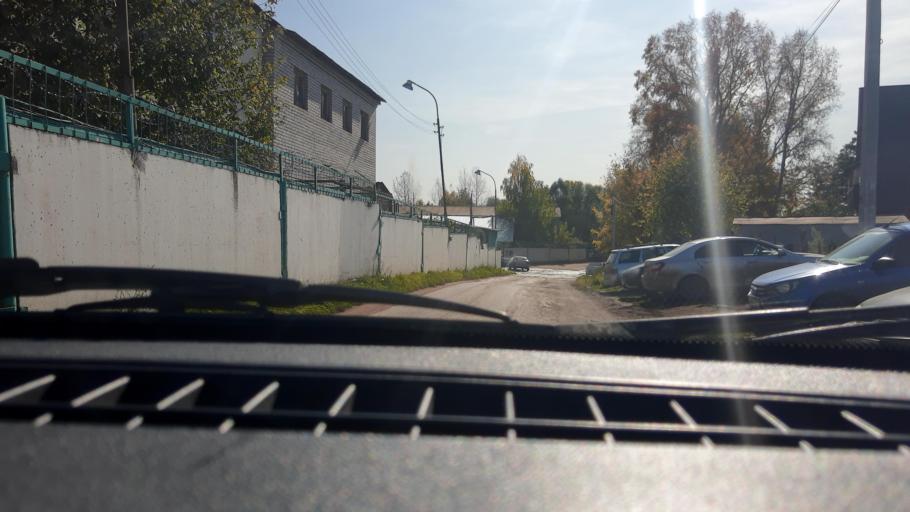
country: RU
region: Bashkortostan
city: Mikhaylovka
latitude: 54.7366
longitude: 55.8297
